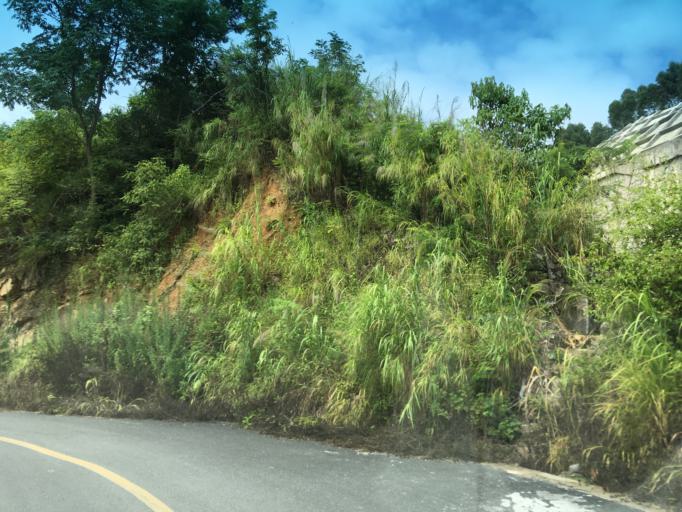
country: CN
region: Guangxi Zhuangzu Zizhiqu
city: Xinzhou
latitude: 24.8197
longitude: 105.6466
